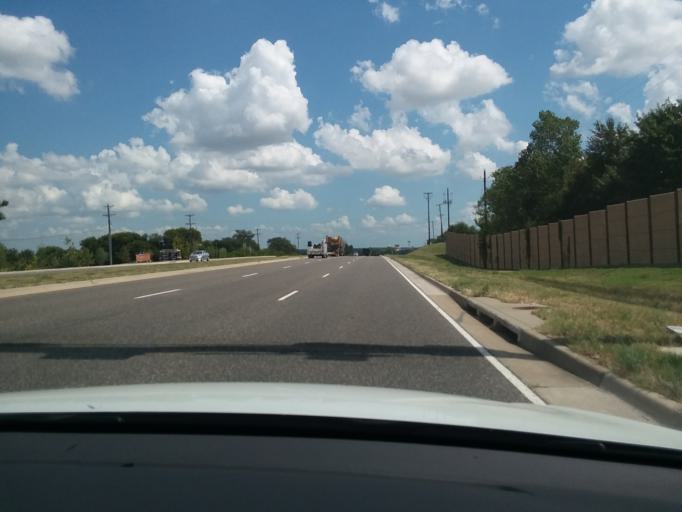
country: US
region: Texas
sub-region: Collin County
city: Prosper
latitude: 33.2189
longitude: -96.7124
